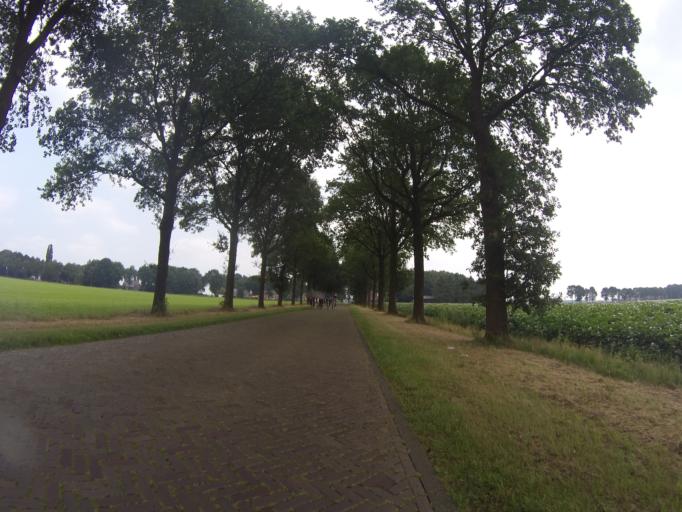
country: NL
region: Drenthe
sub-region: Gemeente Emmen
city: Emmen
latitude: 52.8495
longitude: 6.9176
